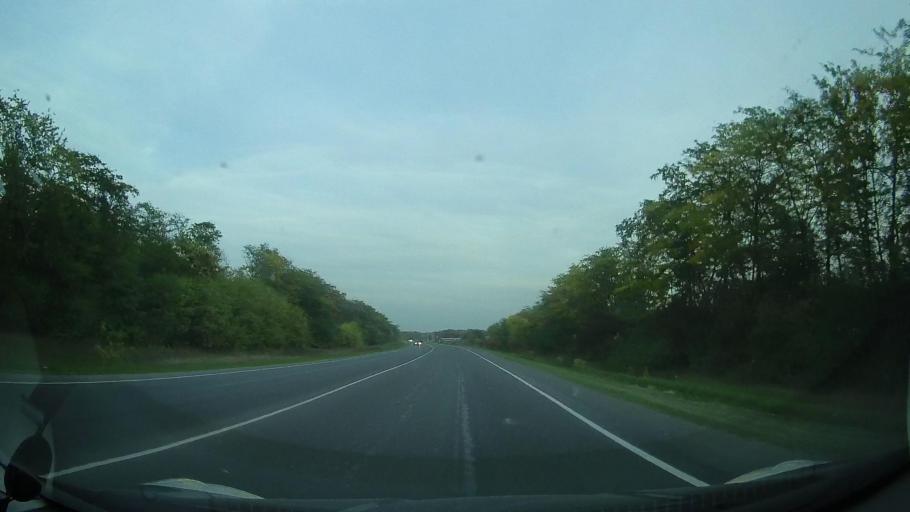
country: RU
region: Rostov
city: Kirovskaya
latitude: 46.9975
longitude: 39.9976
